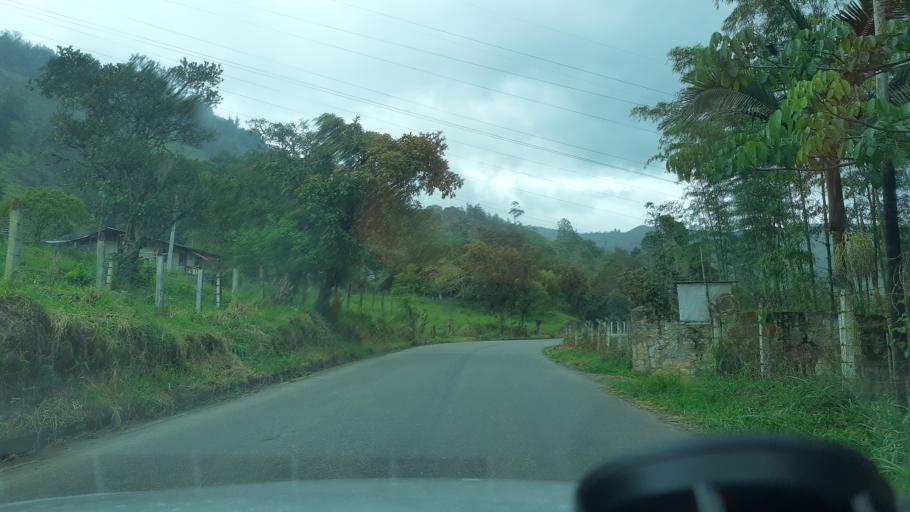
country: CO
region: Boyaca
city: Chinavita
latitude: 5.1716
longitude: -73.3753
